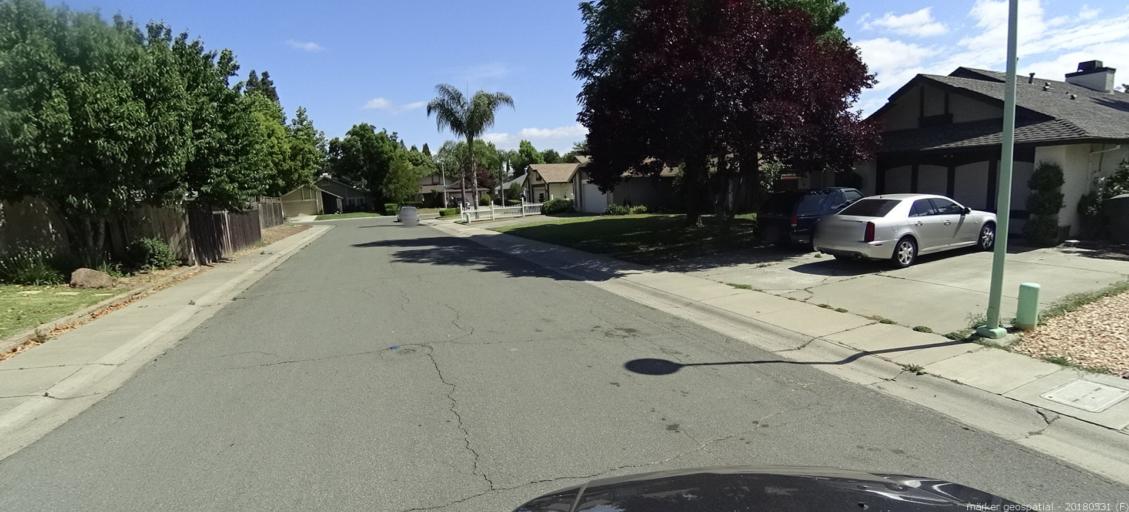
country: US
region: California
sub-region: Sacramento County
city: Sacramento
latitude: 38.6230
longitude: -121.4963
